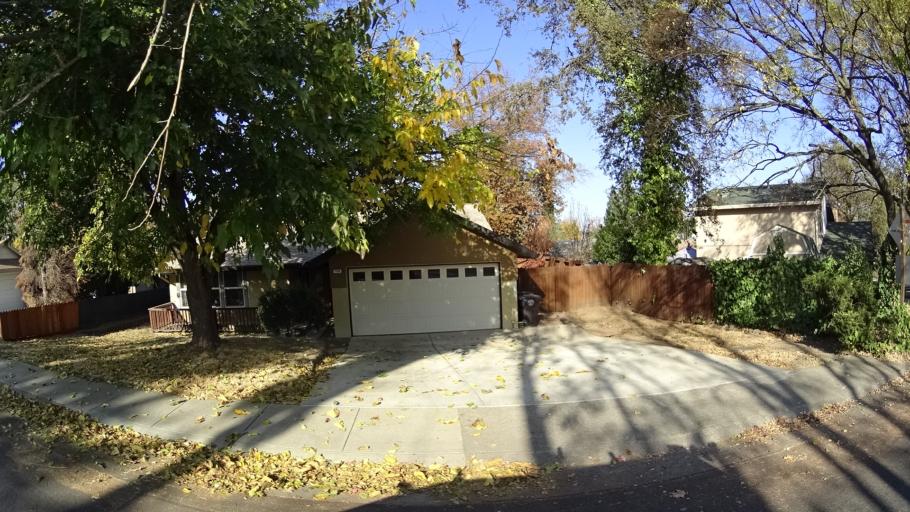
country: US
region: California
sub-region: Sacramento County
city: Fair Oaks
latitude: 38.6752
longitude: -121.2806
